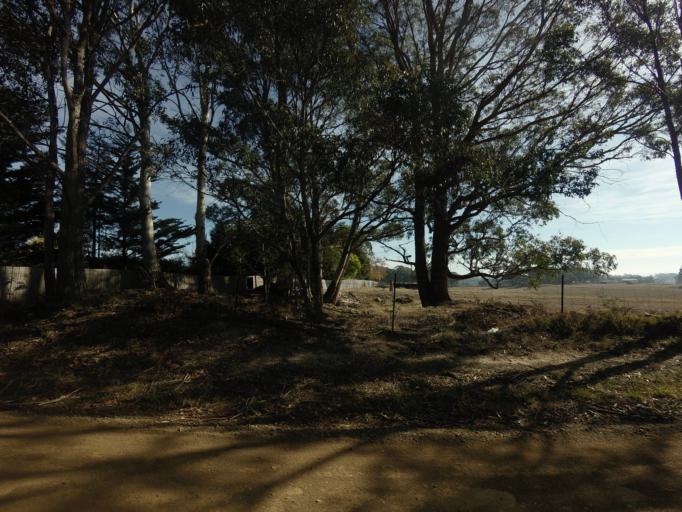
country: AU
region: Tasmania
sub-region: Sorell
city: Sorell
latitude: -42.4769
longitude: 147.4753
